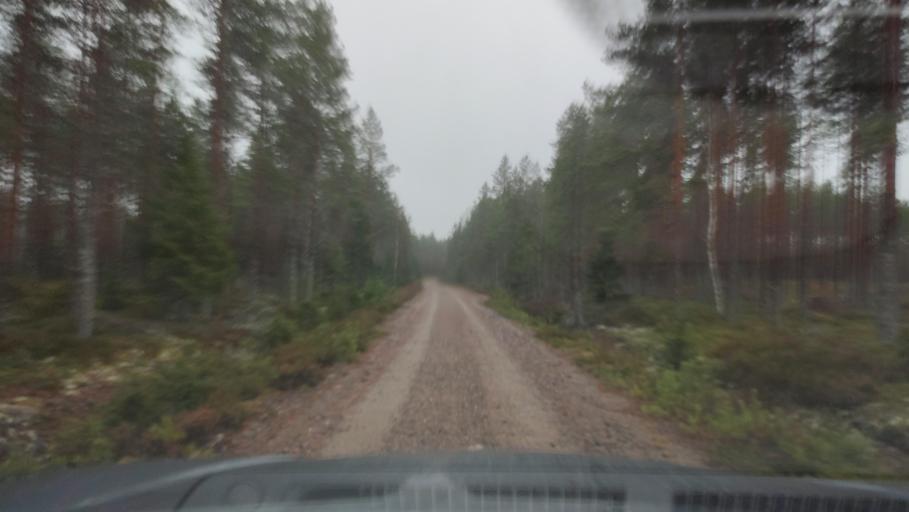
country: FI
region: Southern Ostrobothnia
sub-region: Suupohja
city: Karijoki
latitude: 62.1868
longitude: 21.7371
